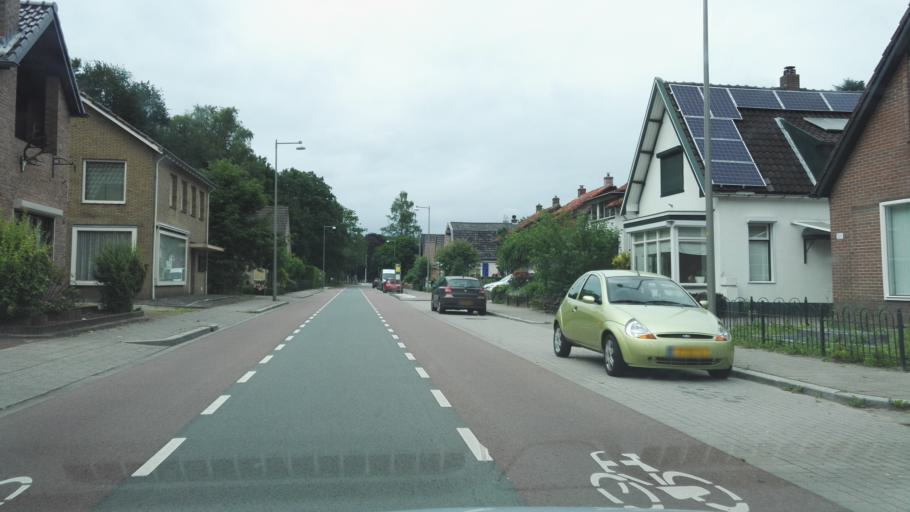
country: NL
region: Gelderland
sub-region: Gemeente Apeldoorn
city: Apeldoorn
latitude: 52.1882
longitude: 5.9436
